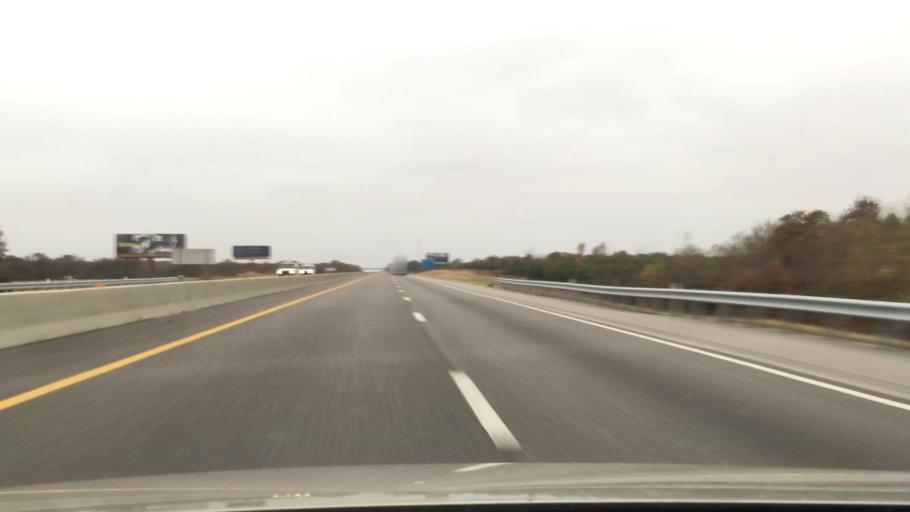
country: US
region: Oklahoma
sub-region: Lincoln County
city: Chandler
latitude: 35.7256
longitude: -96.8509
